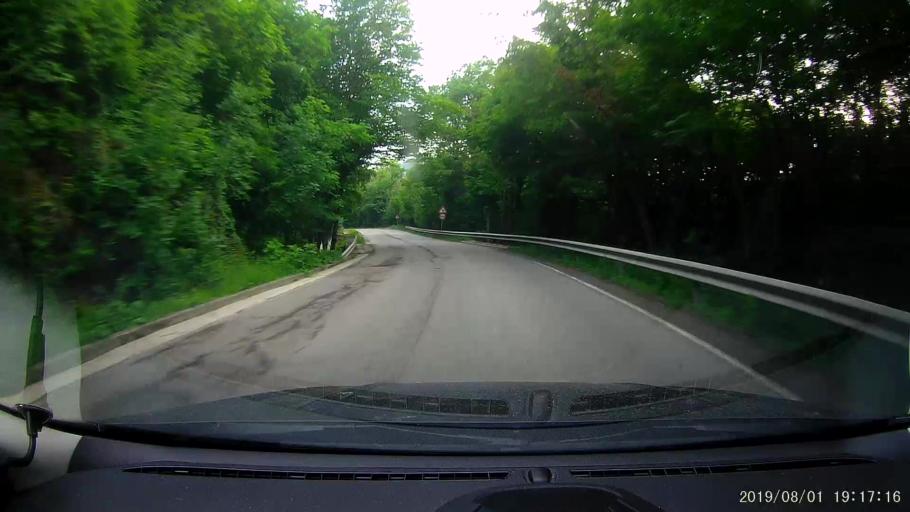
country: BG
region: Shumen
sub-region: Obshtina Smyadovo
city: Smyadovo
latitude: 42.9253
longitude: 26.9439
